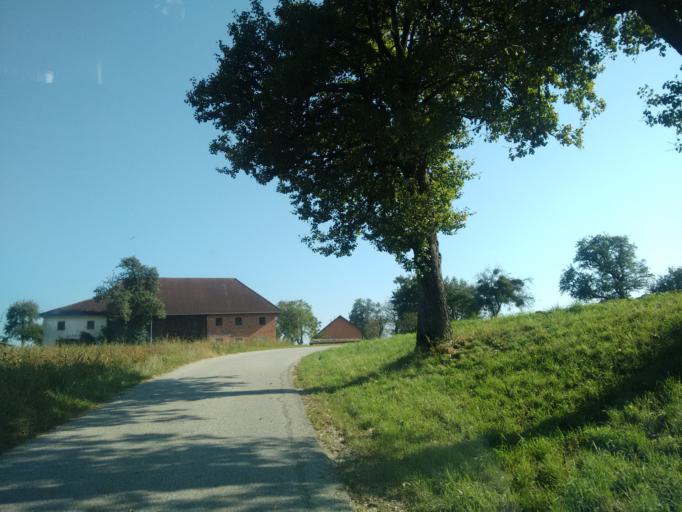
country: AT
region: Upper Austria
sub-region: Politischer Bezirk Linz-Land
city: Horsching
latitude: 48.1341
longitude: 14.2032
